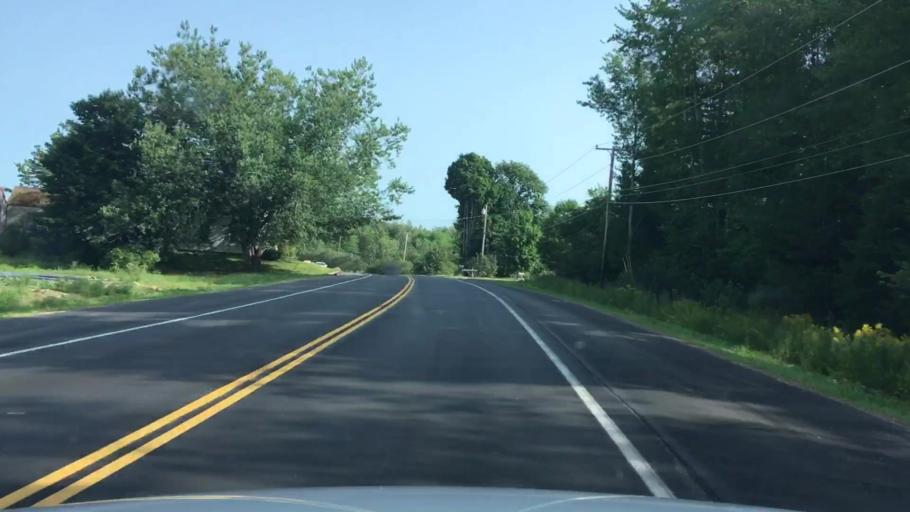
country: US
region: Maine
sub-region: Knox County
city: Warren
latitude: 44.1009
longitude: -69.2487
